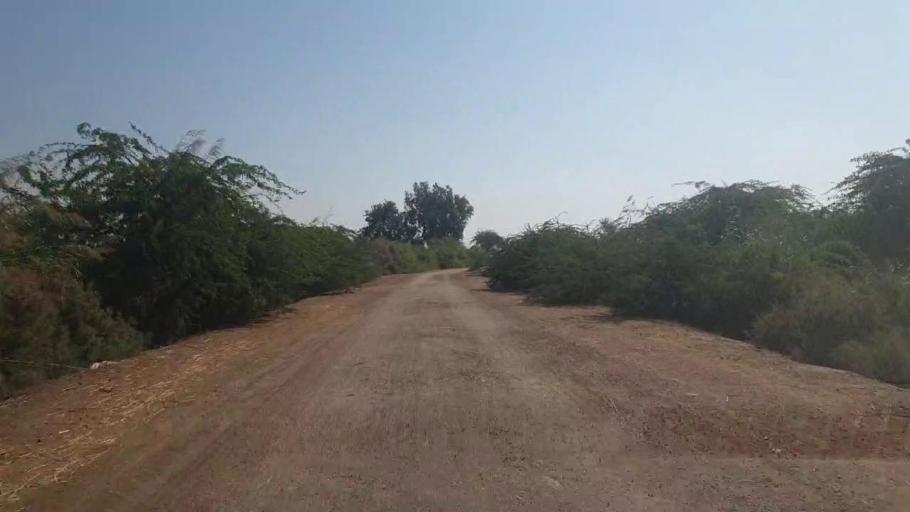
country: PK
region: Sindh
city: Badin
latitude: 24.5711
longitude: 68.8453
